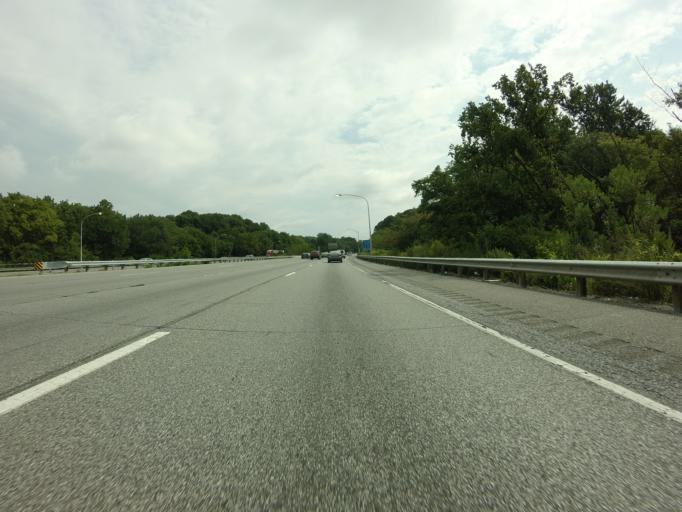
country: US
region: Pennsylvania
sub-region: Delaware County
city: Boothwyn
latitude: 39.8207
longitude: -75.4470
